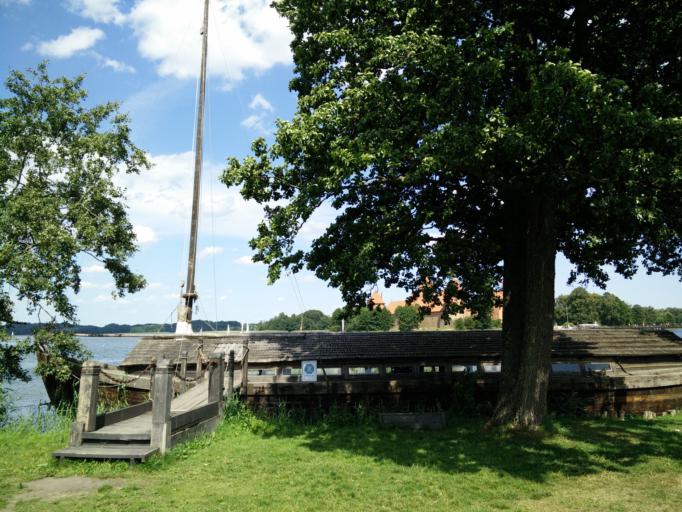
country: LT
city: Trakai
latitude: 54.6501
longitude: 24.9290
